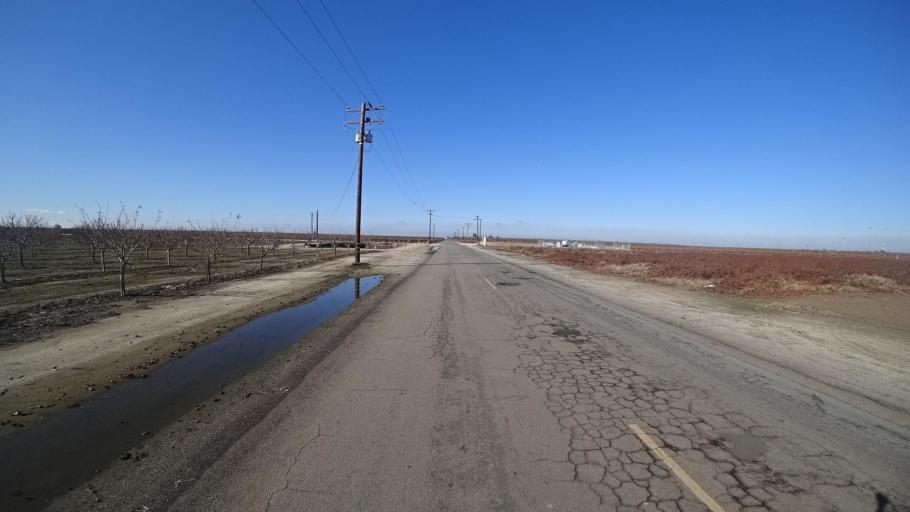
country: US
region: California
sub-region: Kern County
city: Delano
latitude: 35.7325
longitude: -119.2704
